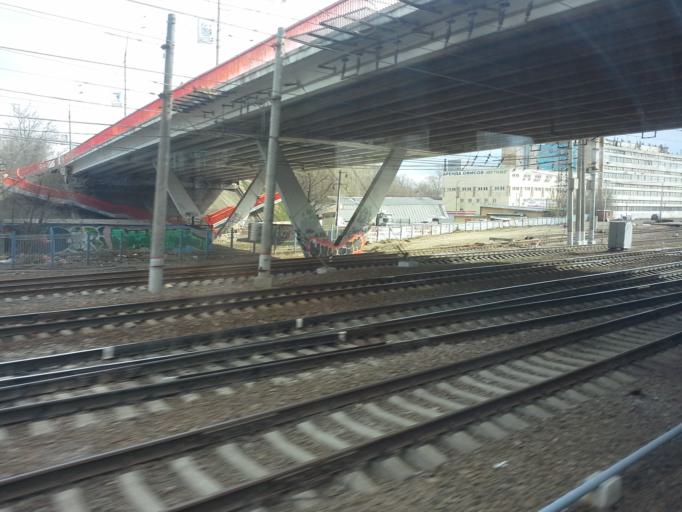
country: RU
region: Moskovskaya
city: Mytishchi
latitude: 55.9188
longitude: 37.7667
